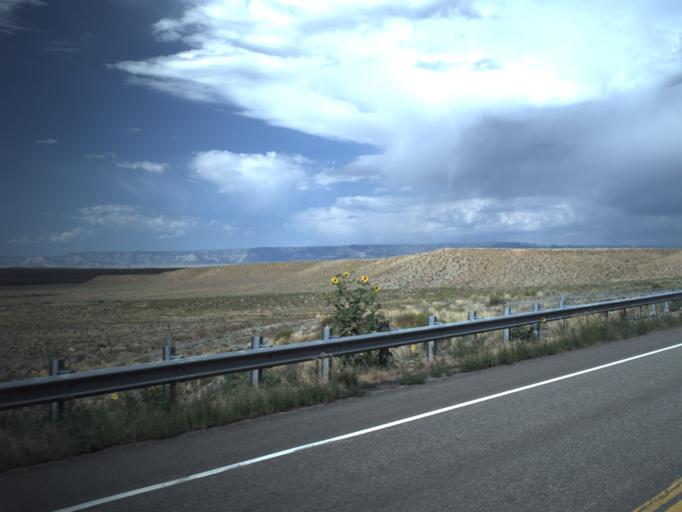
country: US
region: Utah
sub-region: Carbon County
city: East Carbon City
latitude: 39.5159
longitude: -110.5505
